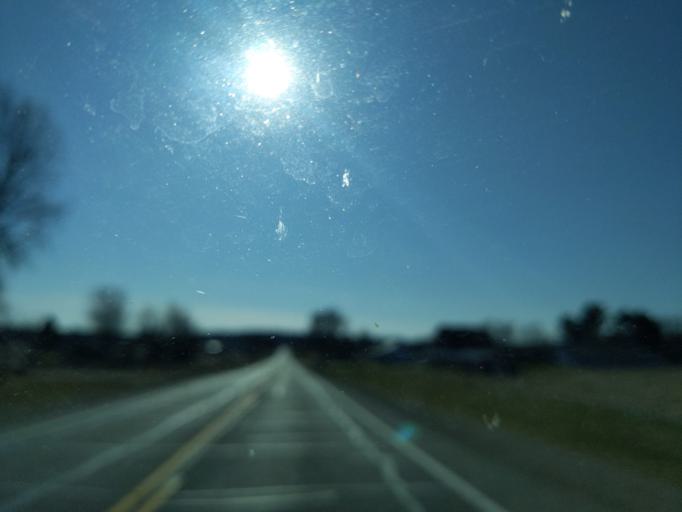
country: US
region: Wisconsin
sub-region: Waushara County
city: Wautoma
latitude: 44.0999
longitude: -89.2897
